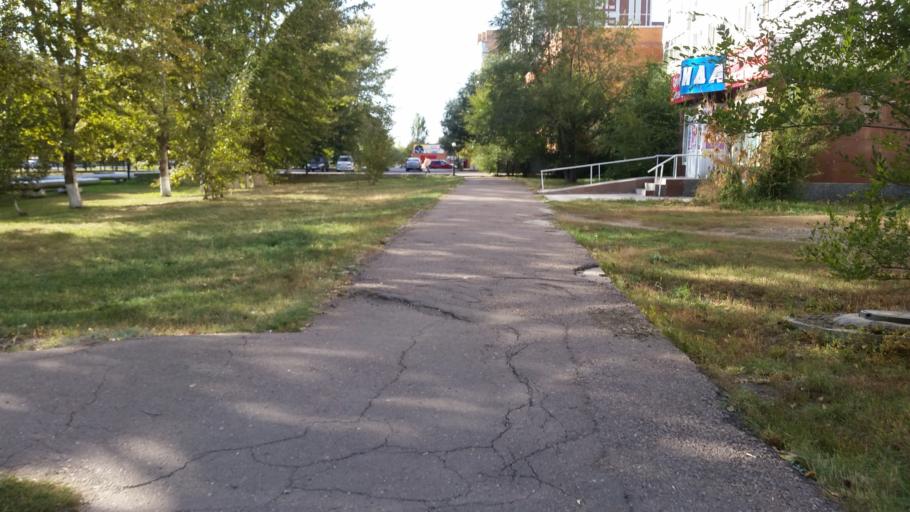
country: KZ
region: Astana Qalasy
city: Astana
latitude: 51.1535
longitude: 71.4906
